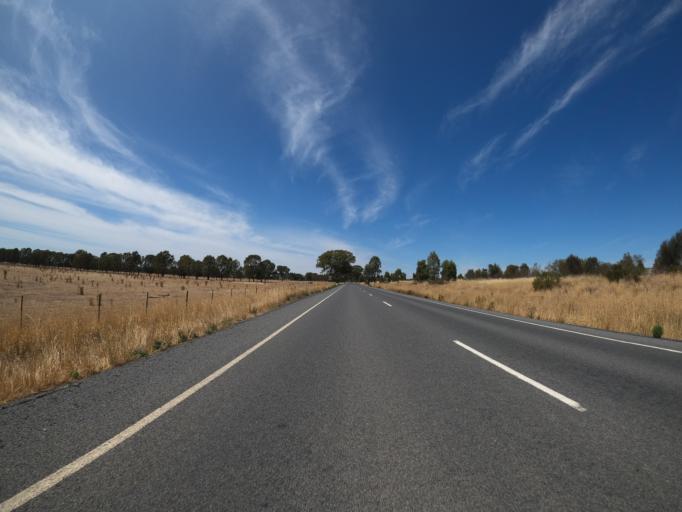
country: AU
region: Victoria
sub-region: Benalla
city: Benalla
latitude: -36.5185
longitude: 146.0336
